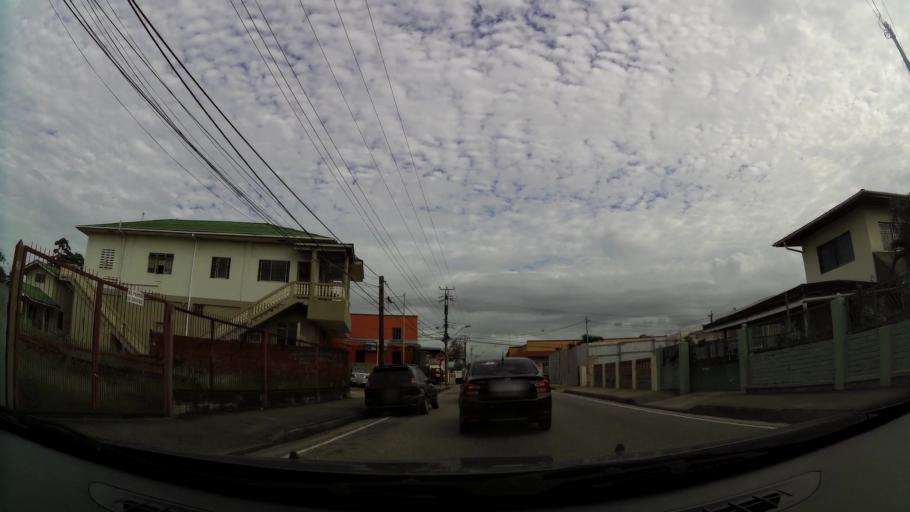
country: TT
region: City of Port of Spain
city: Port-of-Spain
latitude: 10.6621
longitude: -61.5200
